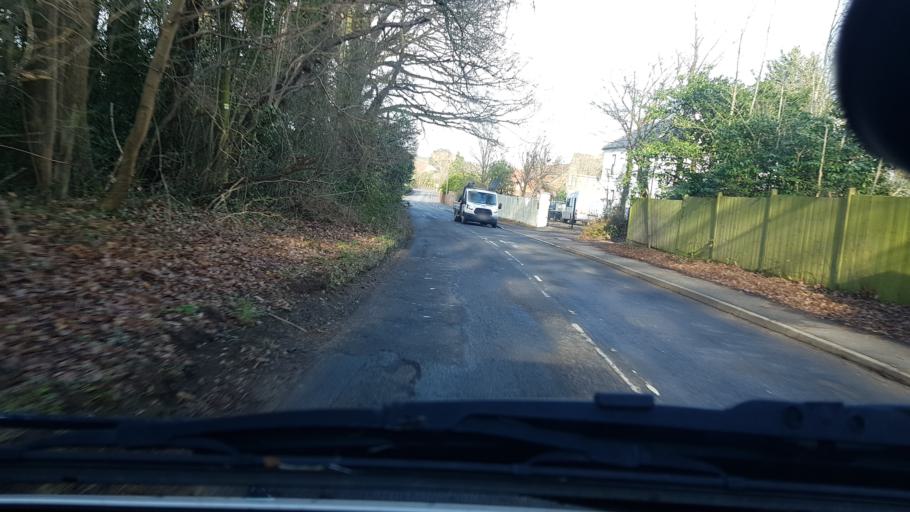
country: GB
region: England
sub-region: Surrey
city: Normandy
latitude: 51.2500
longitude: -0.6681
